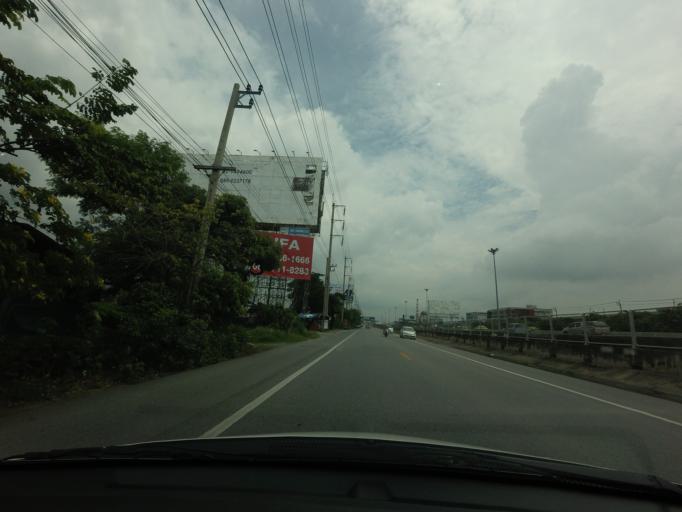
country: TH
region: Bangkok
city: Suan Luang
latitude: 13.7376
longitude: 100.6614
